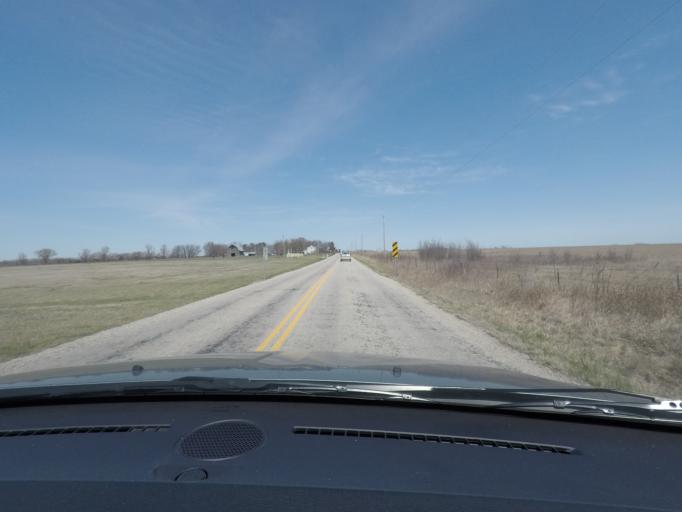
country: US
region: Kansas
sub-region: Lyon County
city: Emporia
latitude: 38.5378
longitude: -96.1700
